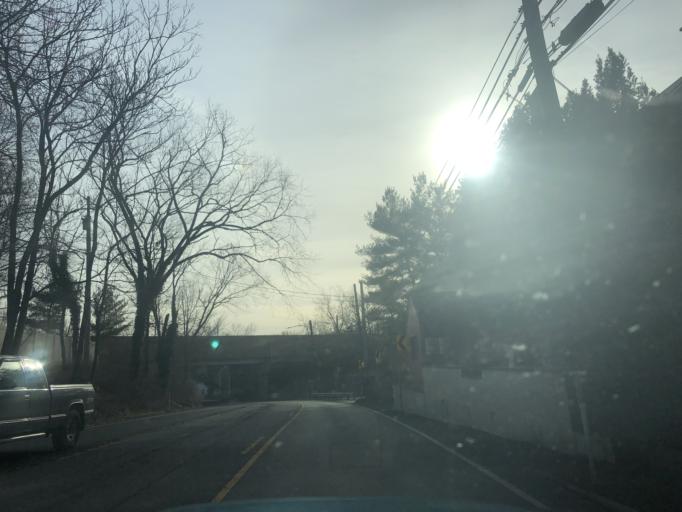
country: US
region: Pennsylvania
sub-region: Montgomery County
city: Fort Washington
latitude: 40.1288
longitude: -75.2177
